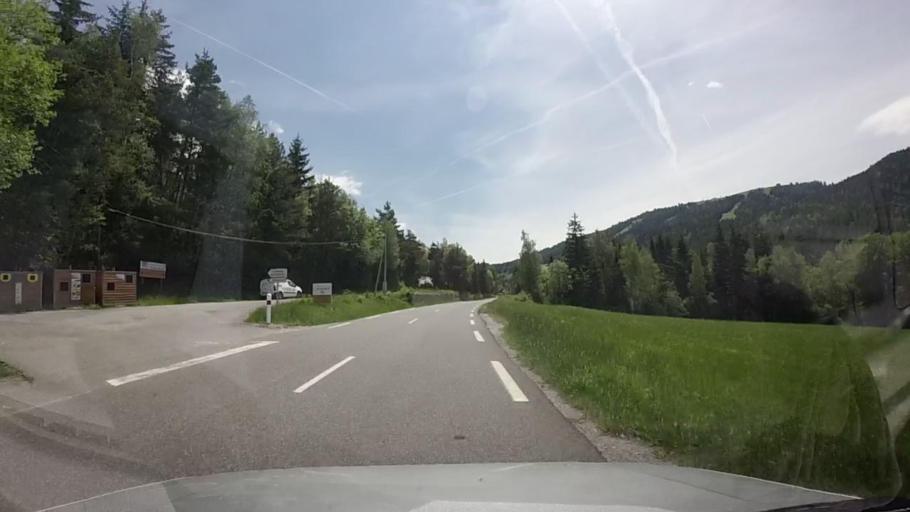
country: FR
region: Provence-Alpes-Cote d'Azur
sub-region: Departement des Alpes-de-Haute-Provence
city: Seyne-les-Alpes
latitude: 44.3323
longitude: 6.3907
